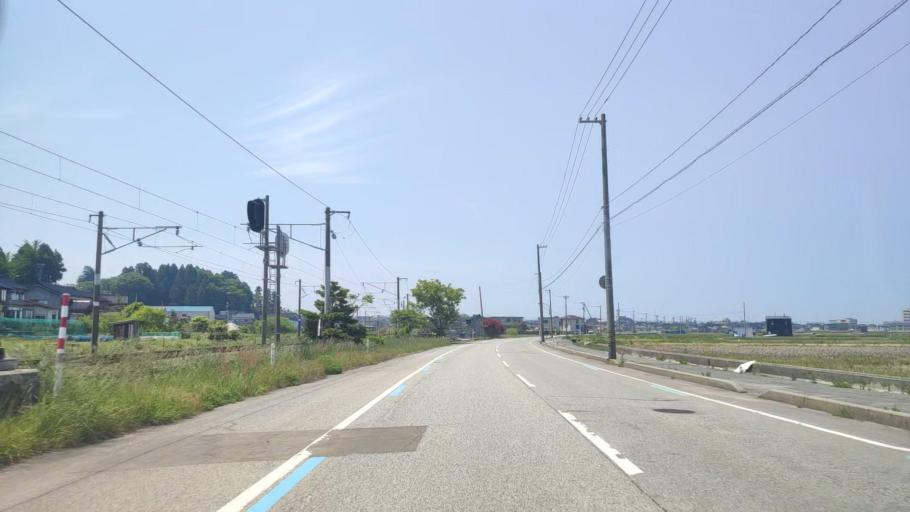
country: JP
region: Toyama
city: Nyuzen
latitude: 36.9628
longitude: 137.5737
